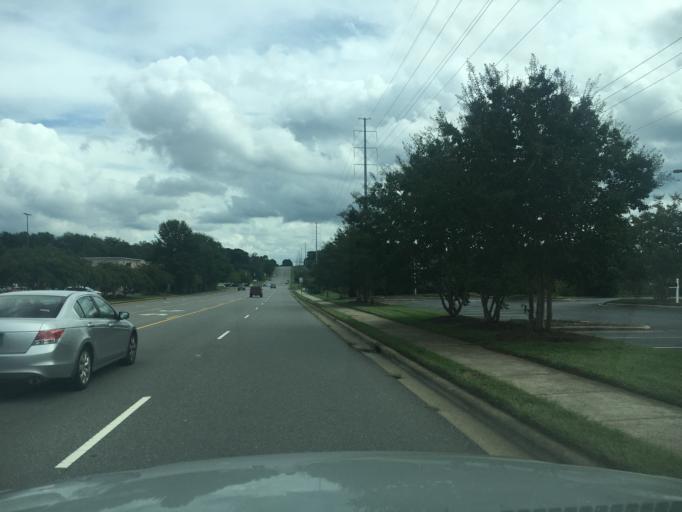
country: US
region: North Carolina
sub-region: Catawba County
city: Hickory
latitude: 35.7012
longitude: -81.3048
